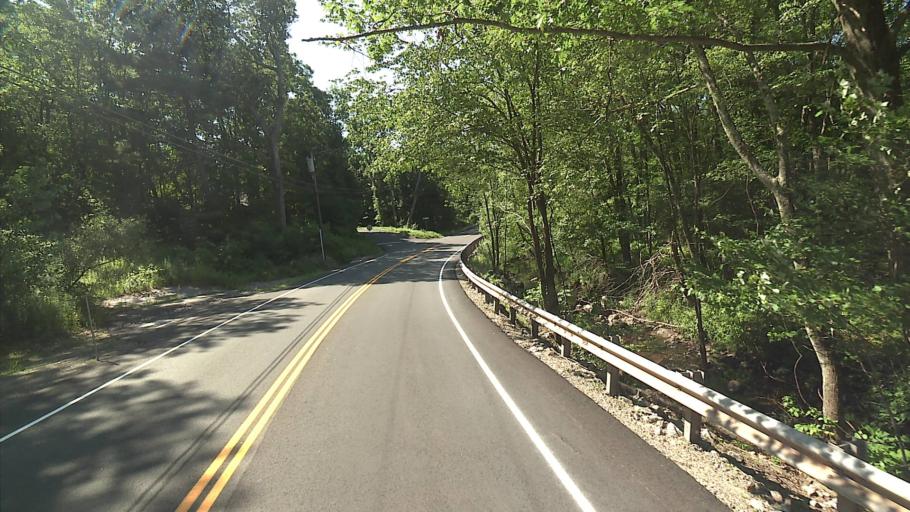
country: US
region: Connecticut
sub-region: Litchfield County
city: Terryville
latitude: 41.7159
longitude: -73.0117
